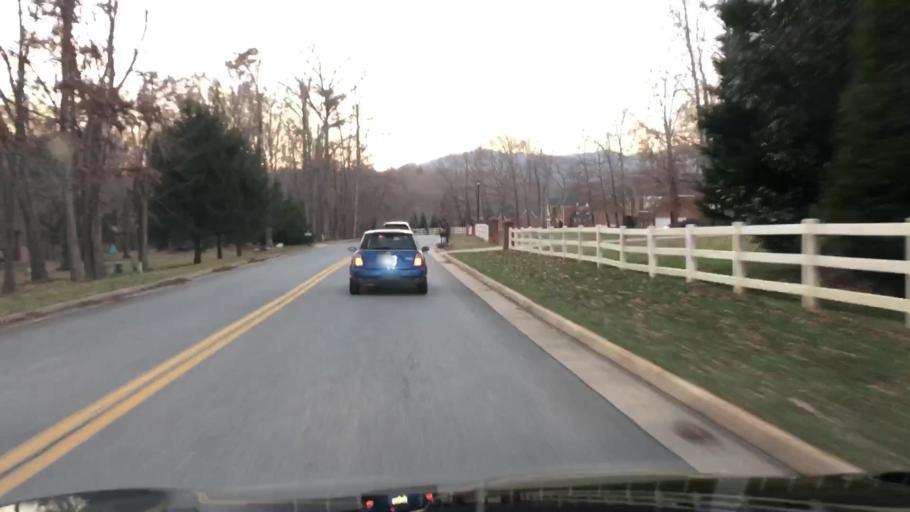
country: US
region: Virginia
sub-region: Bedford County
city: Forest
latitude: 37.4315
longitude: -79.2527
